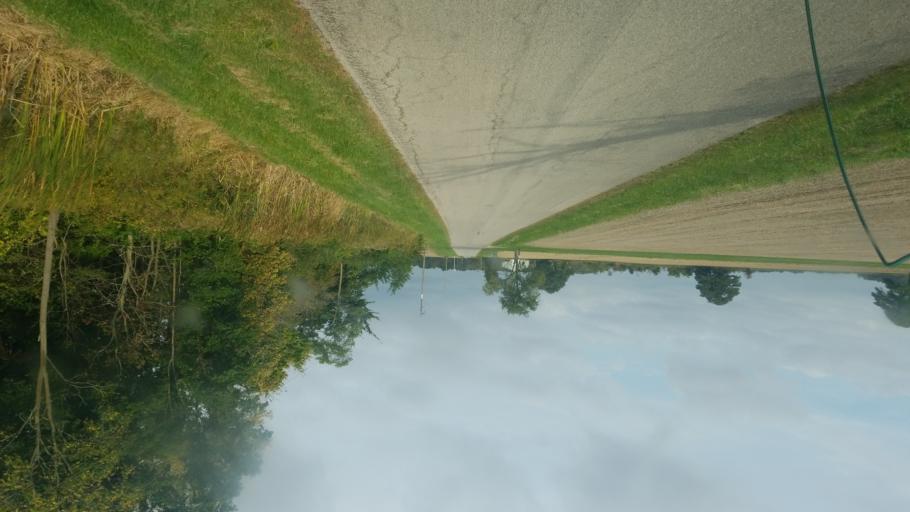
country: US
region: Ohio
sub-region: Seneca County
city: Fostoria
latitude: 41.0501
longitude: -83.4876
